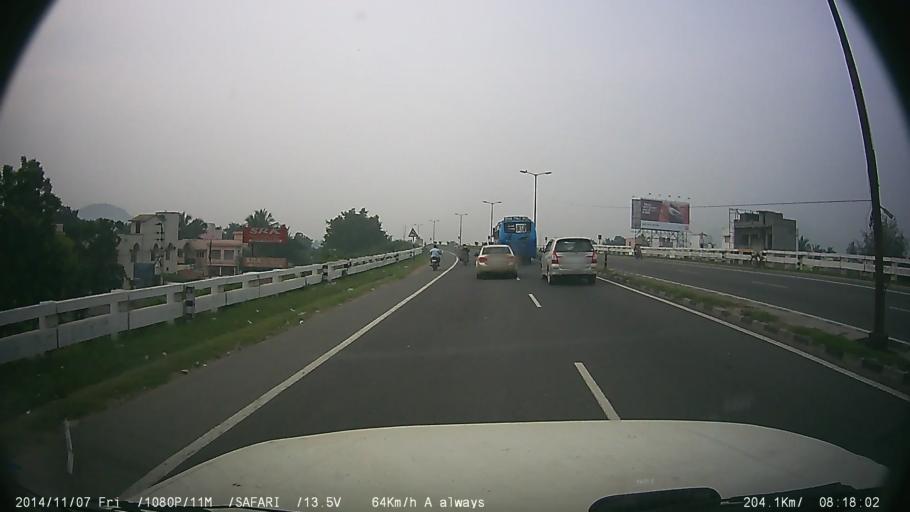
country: IN
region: Tamil Nadu
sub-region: Salem
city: Salem
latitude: 11.6633
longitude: 78.1224
